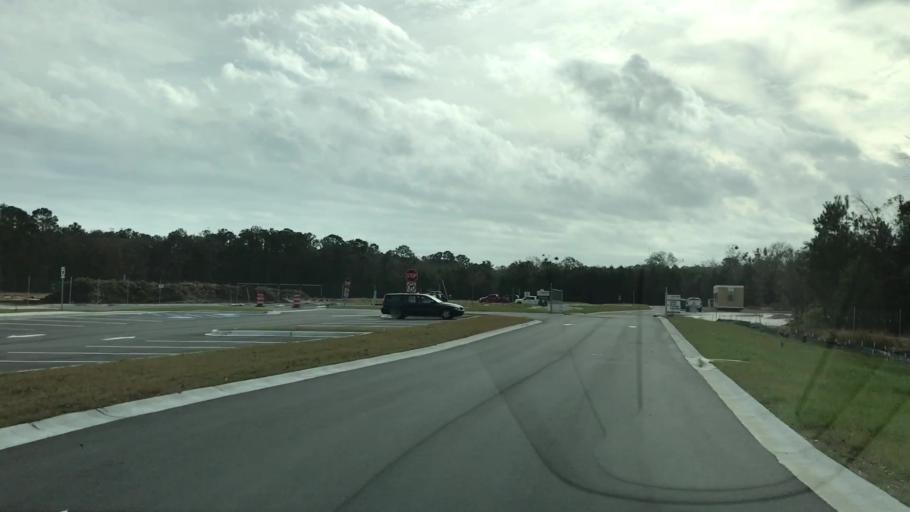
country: US
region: South Carolina
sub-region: Beaufort County
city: Burton
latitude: 32.4140
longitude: -80.7474
